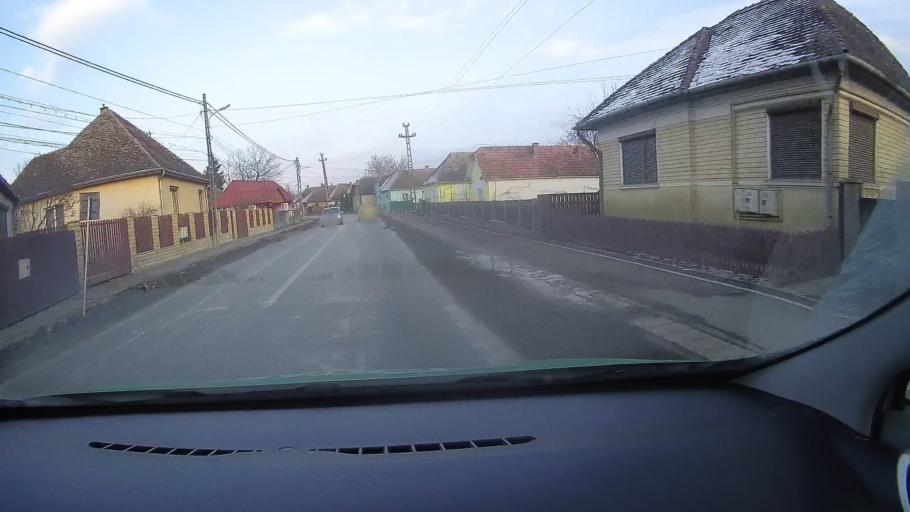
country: RO
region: Harghita
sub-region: Oras Cristuru Secuiesc
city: Cristuru Secuiesc
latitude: 46.2824
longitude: 25.0225
